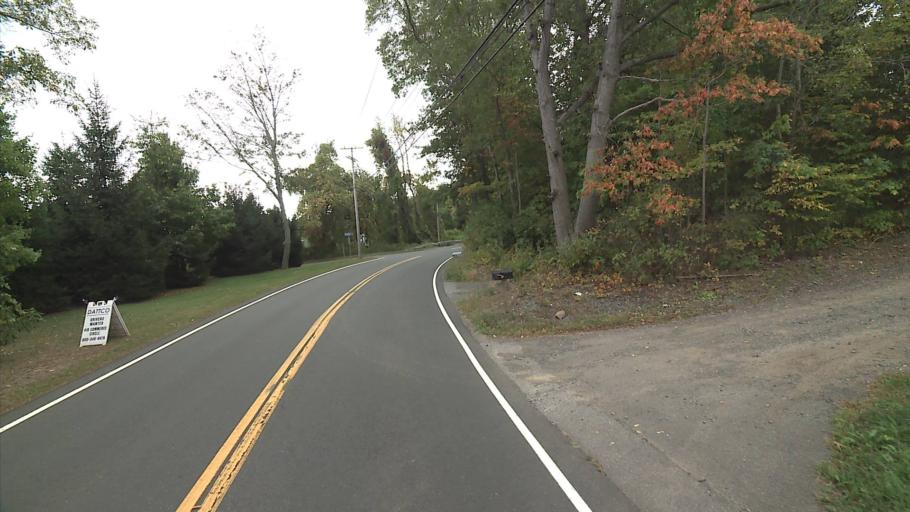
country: US
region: Connecticut
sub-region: Middlesex County
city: Durham
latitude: 41.4828
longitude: -72.7242
